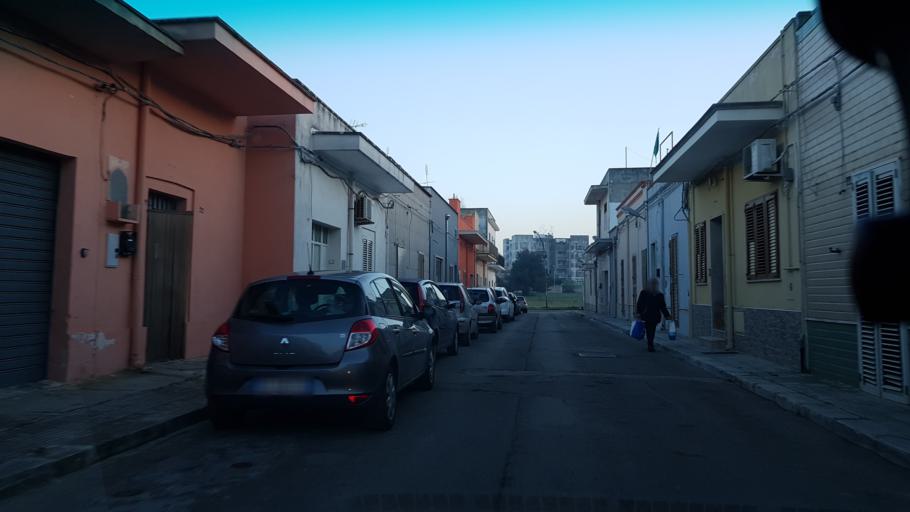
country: IT
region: Apulia
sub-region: Provincia di Brindisi
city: Mesagne
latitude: 40.5623
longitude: 17.7957
